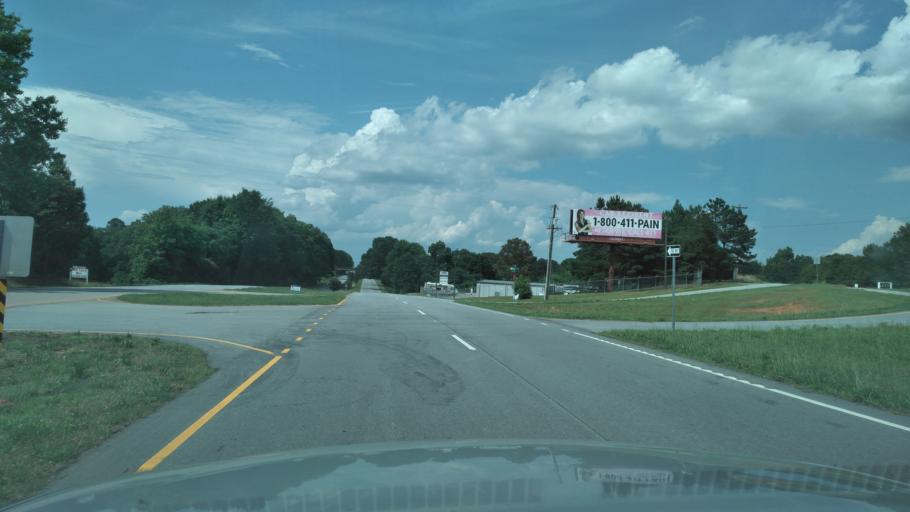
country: US
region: South Carolina
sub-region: Spartanburg County
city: Roebuck
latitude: 34.8624
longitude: -81.9617
